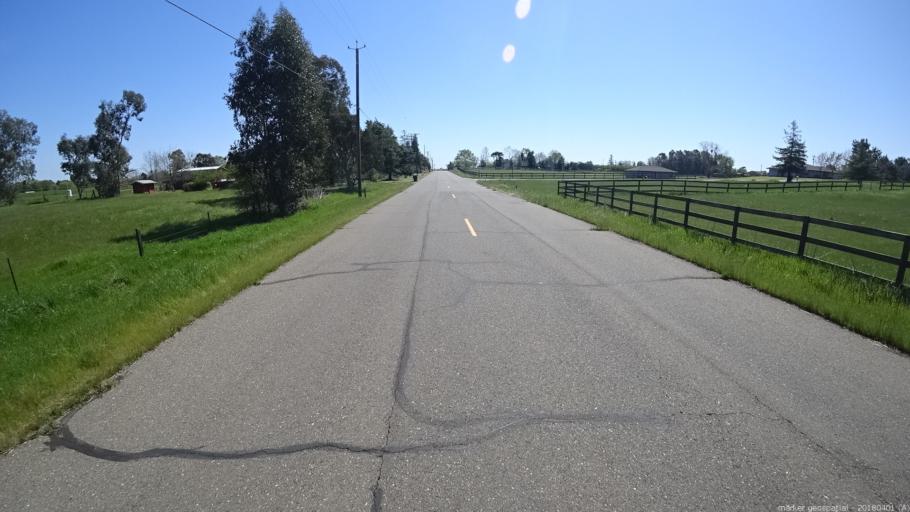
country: US
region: California
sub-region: Sacramento County
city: Wilton
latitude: 38.4165
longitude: -121.2102
